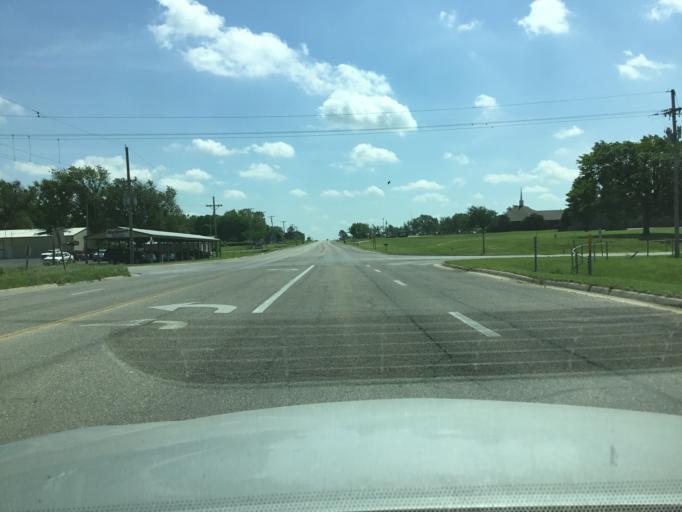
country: US
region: Kansas
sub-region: Labette County
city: Parsons
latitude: 37.3402
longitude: -95.2316
